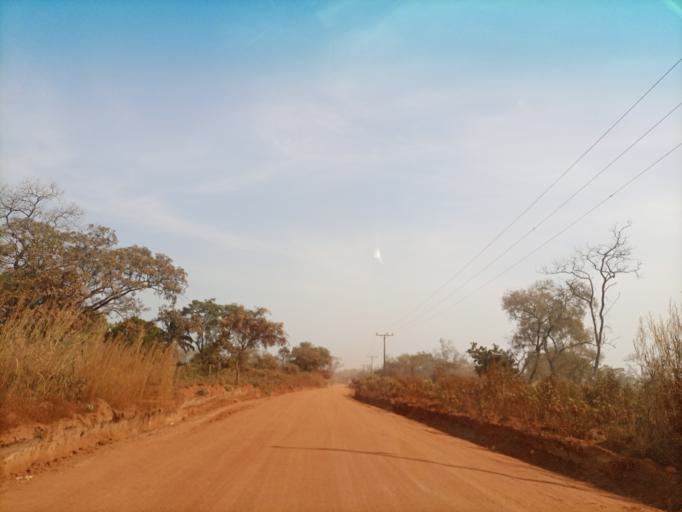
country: NG
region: Enugu
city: Eha Amufu
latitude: 6.6726
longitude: 7.7349
